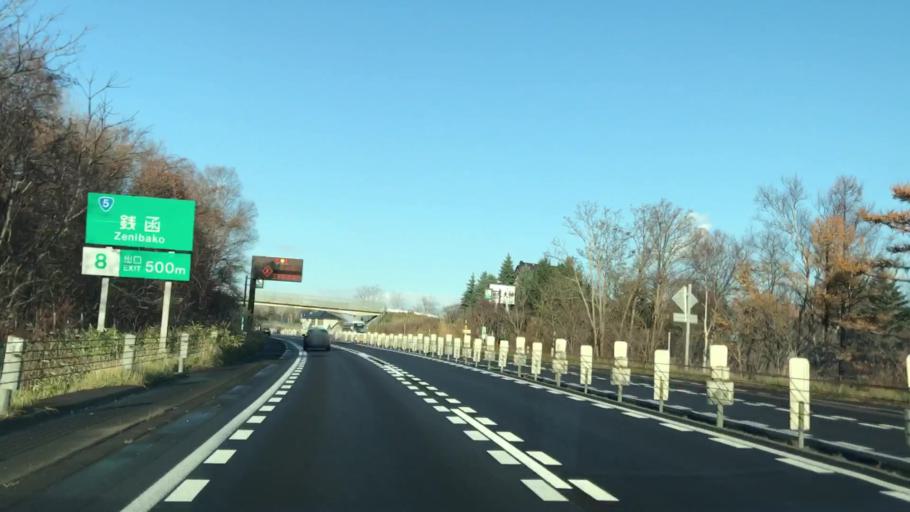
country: JP
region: Hokkaido
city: Sapporo
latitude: 43.1315
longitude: 141.1823
